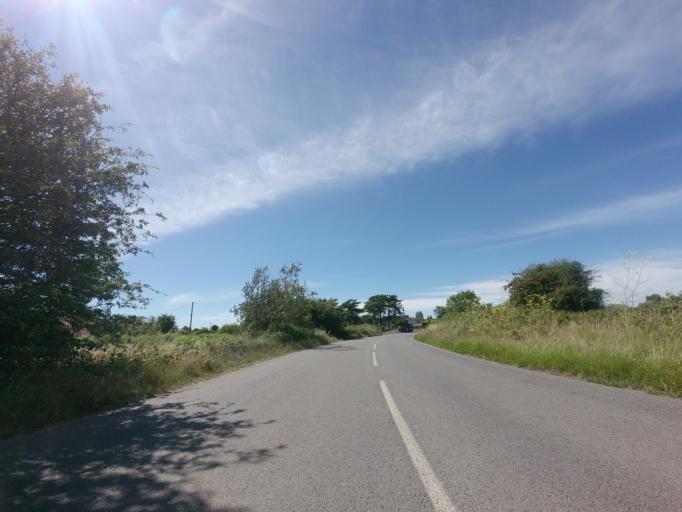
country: GB
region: England
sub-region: Kent
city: Sandwich
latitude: 51.2695
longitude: 1.3639
